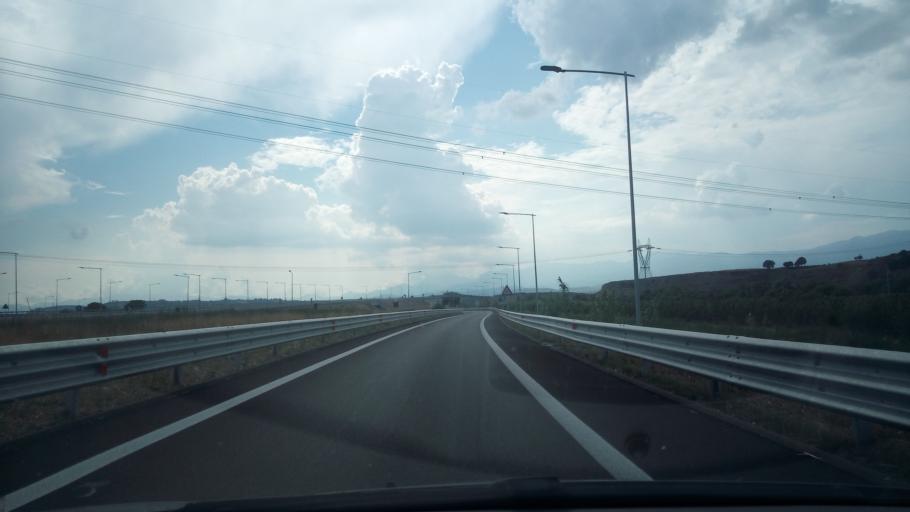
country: IT
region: Calabria
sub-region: Provincia di Cosenza
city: Doria
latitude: 39.7247
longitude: 16.3193
